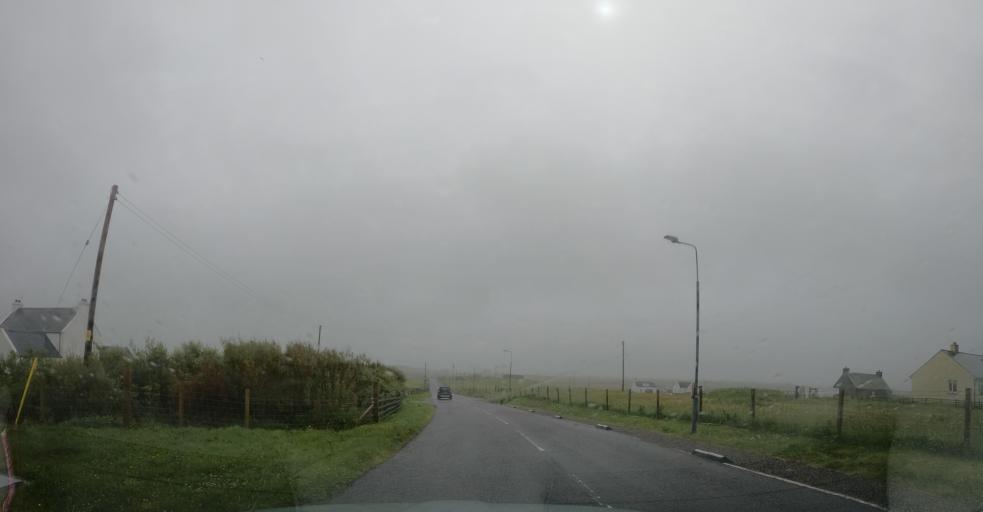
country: GB
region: Scotland
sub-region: Eilean Siar
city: Benbecula
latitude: 57.4725
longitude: -7.3738
